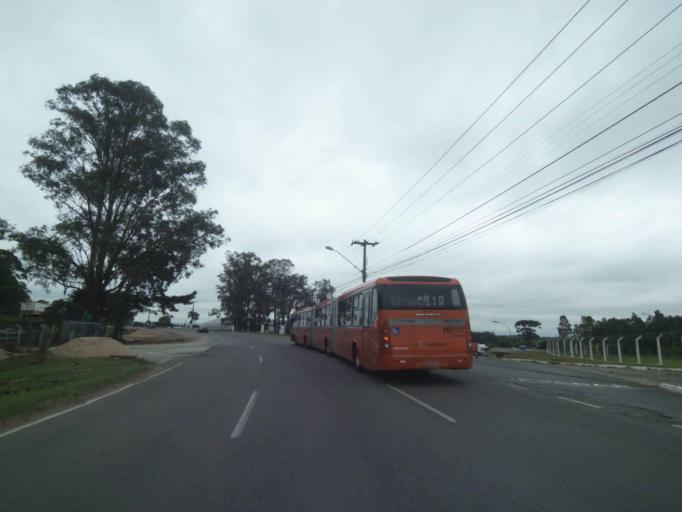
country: BR
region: Parana
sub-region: Sao Jose Dos Pinhais
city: Sao Jose dos Pinhais
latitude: -25.5384
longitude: -49.3099
